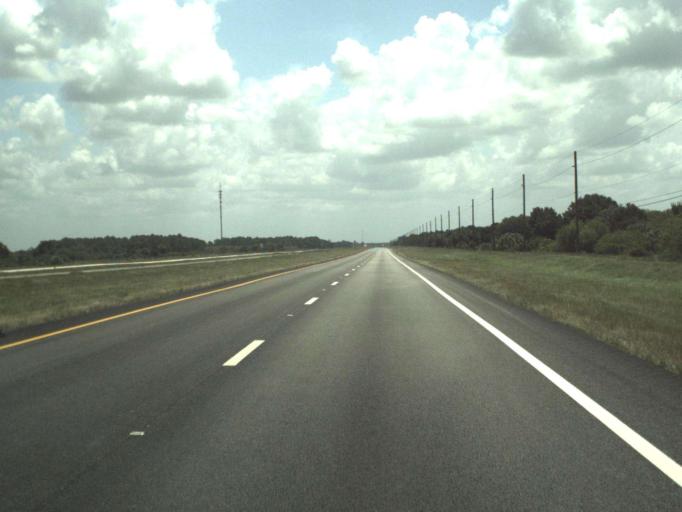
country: US
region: Florida
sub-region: Okeechobee County
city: Cypress Quarters
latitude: 27.3605
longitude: -80.6237
